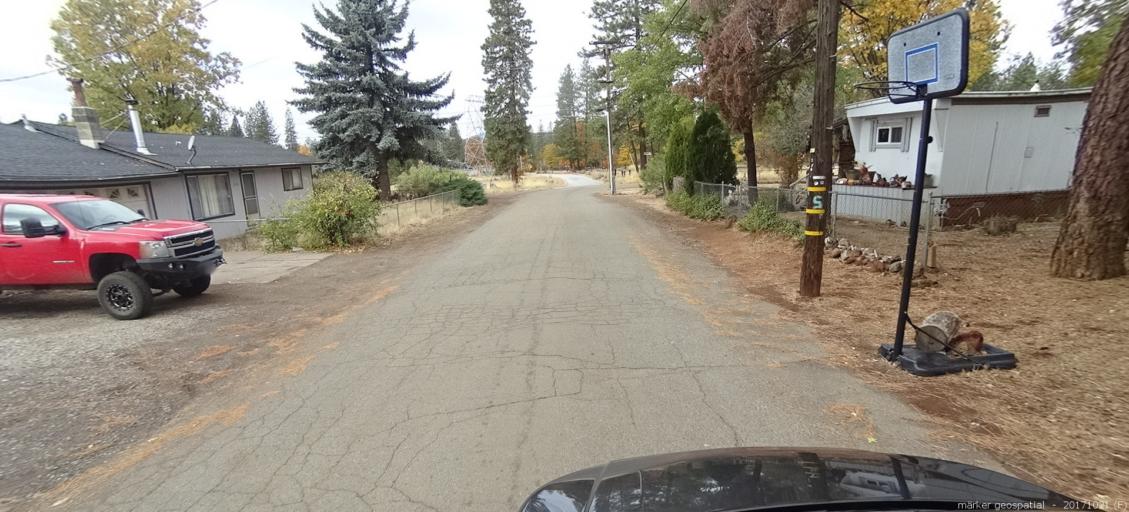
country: US
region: California
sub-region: Shasta County
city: Burney
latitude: 40.9212
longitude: -121.6266
